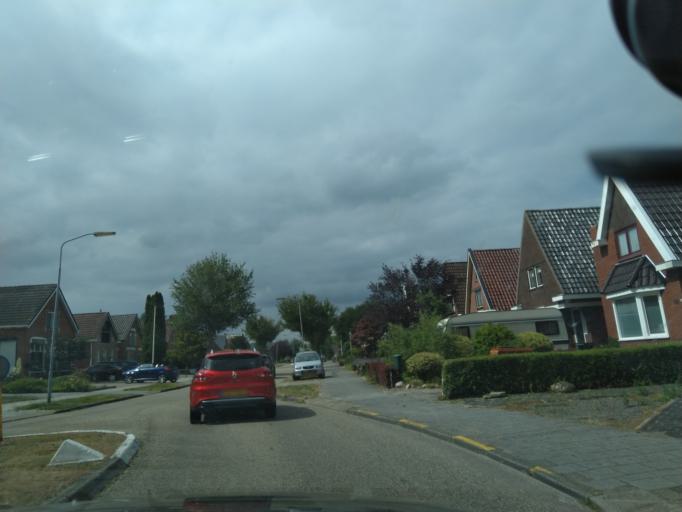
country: NL
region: Groningen
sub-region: Gemeente Pekela
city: Oude Pekela
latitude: 53.0773
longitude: 6.9737
